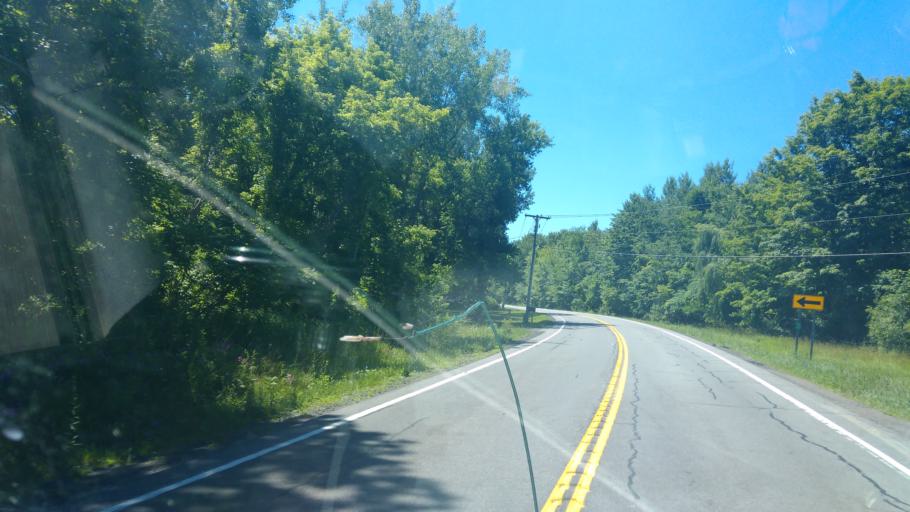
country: US
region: New York
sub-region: Wayne County
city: Sodus
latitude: 43.1893
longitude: -76.9881
